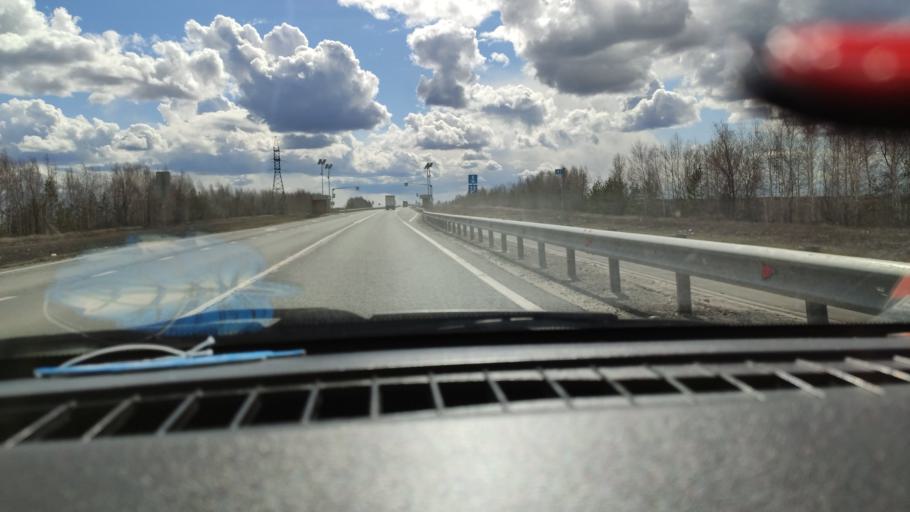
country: RU
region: Saratov
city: Dukhovnitskoye
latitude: 52.8385
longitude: 48.2445
